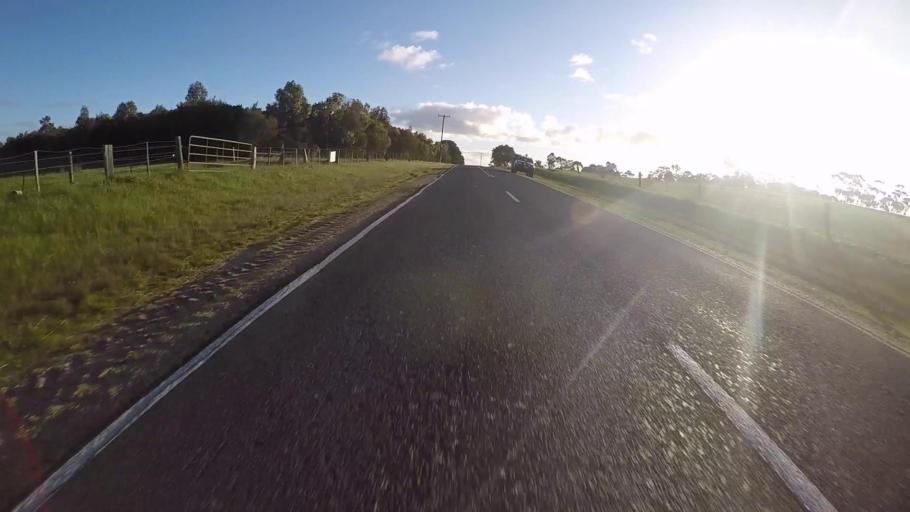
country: AU
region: Victoria
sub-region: Greater Geelong
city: Wandana Heights
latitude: -38.1705
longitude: 144.2070
